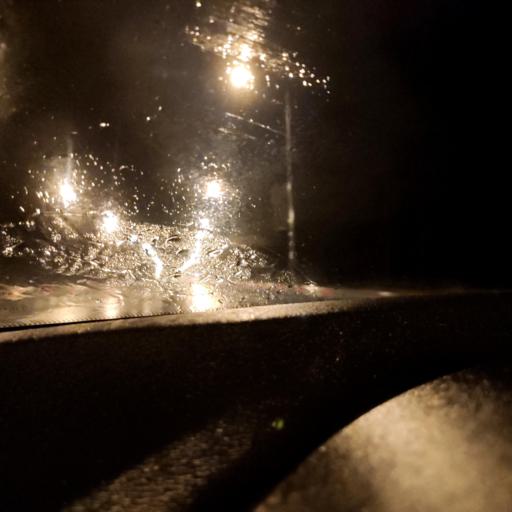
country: RU
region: Samara
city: Petra-Dubrava
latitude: 53.3017
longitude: 50.2418
